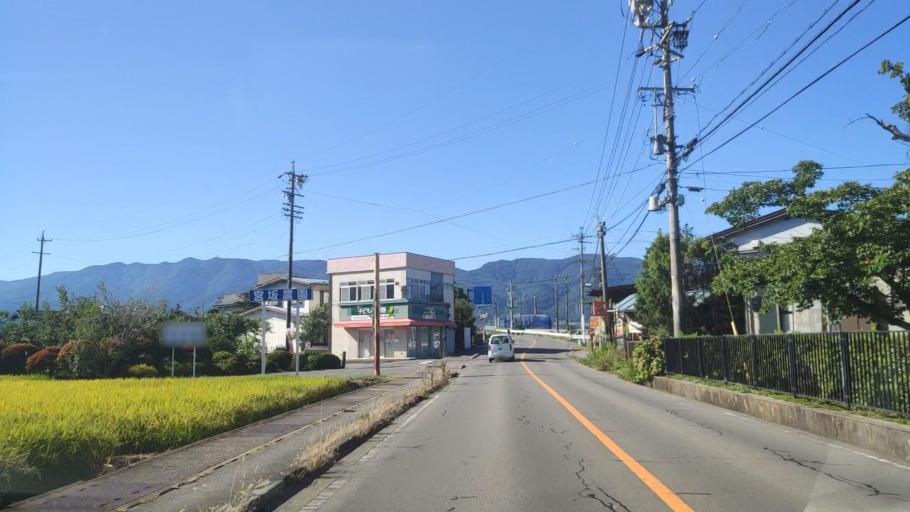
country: JP
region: Nagano
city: Suwa
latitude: 36.0334
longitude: 138.1095
